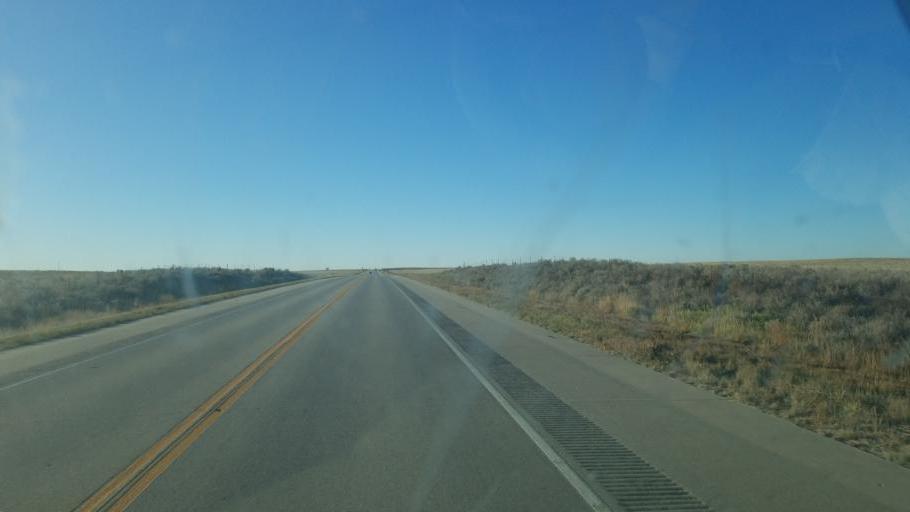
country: US
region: Colorado
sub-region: Kiowa County
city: Eads
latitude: 38.5400
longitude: -102.7859
